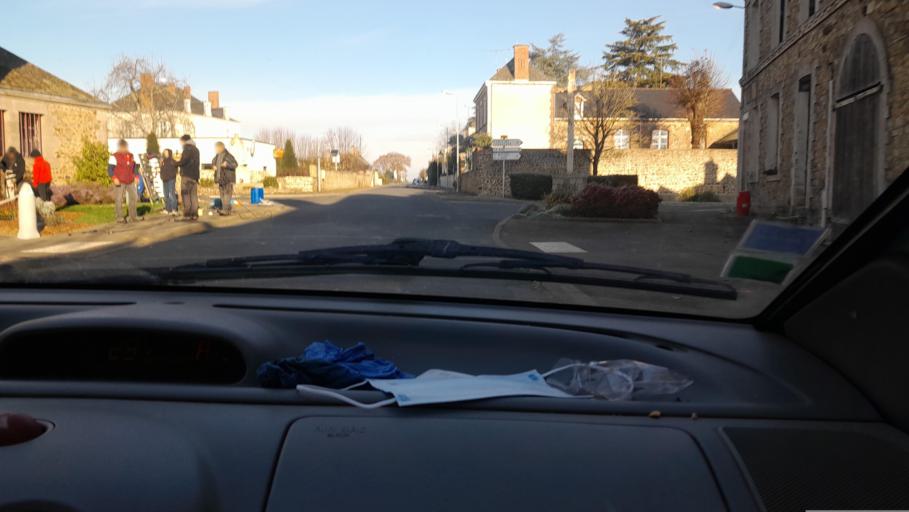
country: FR
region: Brittany
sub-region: Departement d'Ille-et-Vilaine
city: Rannee
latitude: 47.8864
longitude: -1.1816
